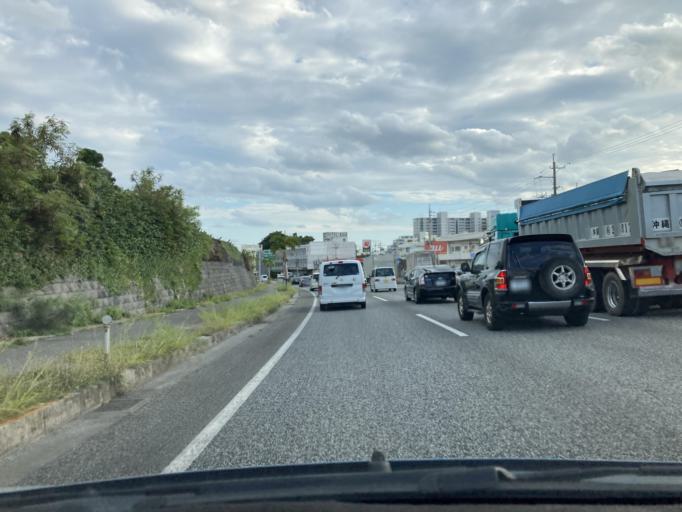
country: JP
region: Okinawa
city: Chatan
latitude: 26.3296
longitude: 127.7519
